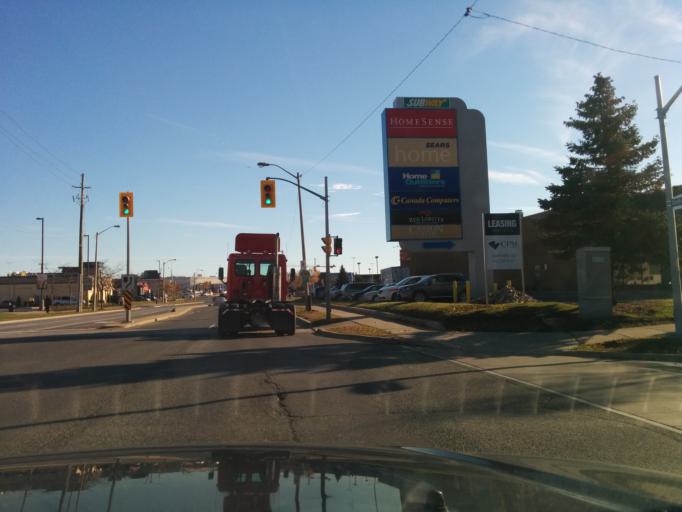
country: CA
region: Ontario
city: Etobicoke
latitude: 43.6162
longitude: -79.5571
